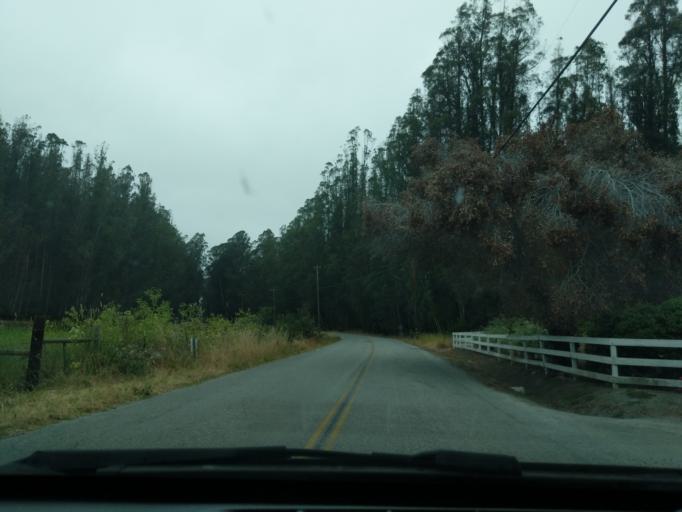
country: US
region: California
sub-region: San Benito County
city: Aromas
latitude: 36.8904
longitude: -121.6016
